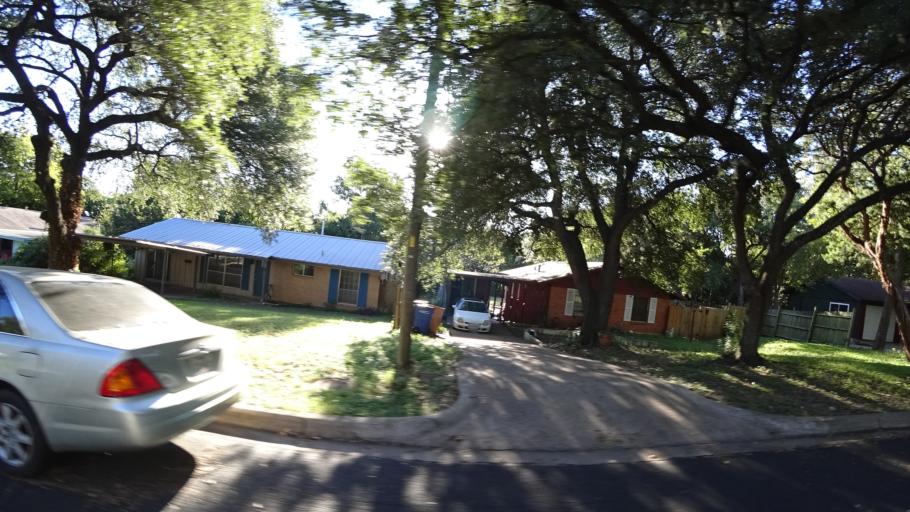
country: US
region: Texas
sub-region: Travis County
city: Austin
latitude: 30.2283
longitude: -97.7643
